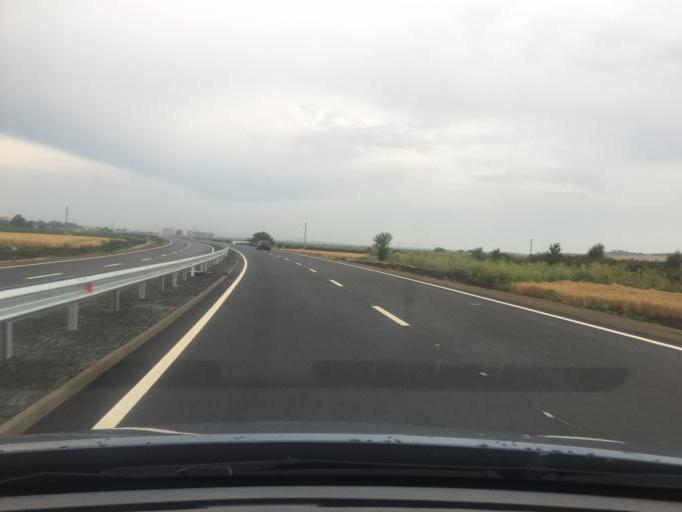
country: BG
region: Burgas
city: Aheloy
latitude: 42.6515
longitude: 27.6374
